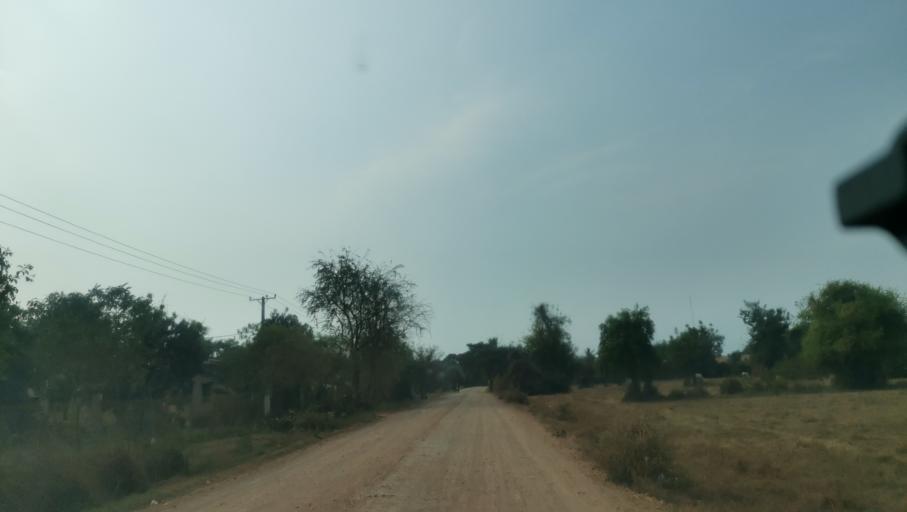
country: KH
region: Battambang
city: Battambang
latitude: 13.0698
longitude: 103.1693
